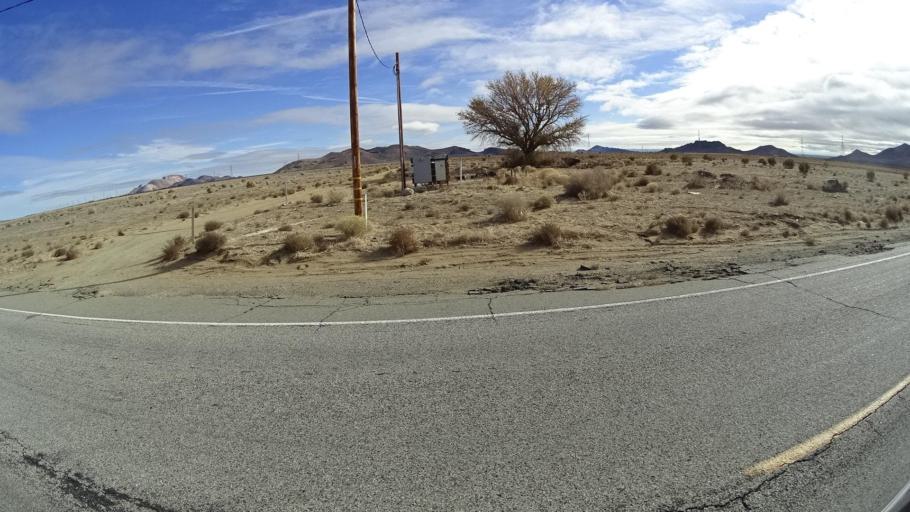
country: US
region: California
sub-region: Kern County
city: Rosamond
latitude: 34.9145
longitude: -118.2914
